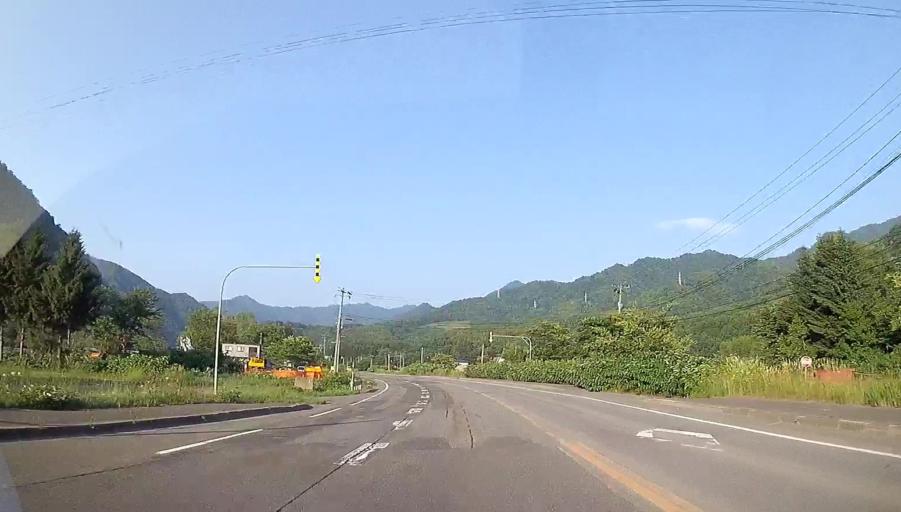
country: JP
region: Hokkaido
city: Shimo-furano
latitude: 42.8943
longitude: 142.5522
